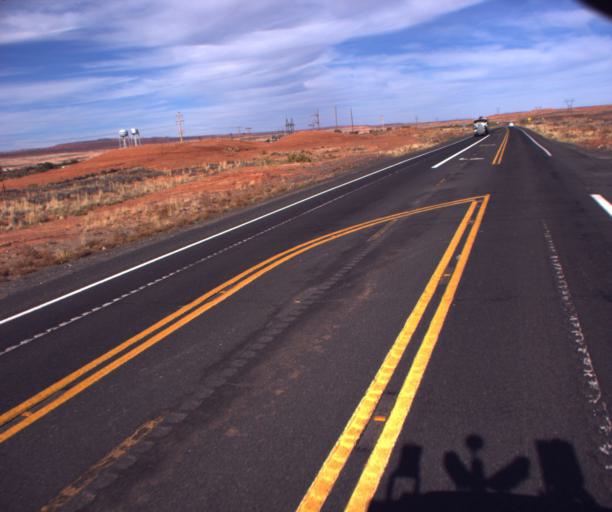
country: US
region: Arizona
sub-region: Navajo County
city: Kayenta
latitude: 36.8379
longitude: -109.8480
